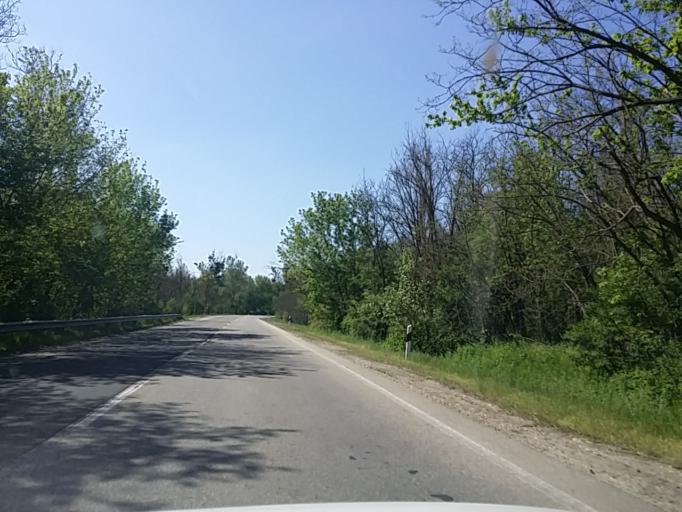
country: HU
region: Pest
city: Godollo
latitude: 47.6033
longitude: 19.4044
